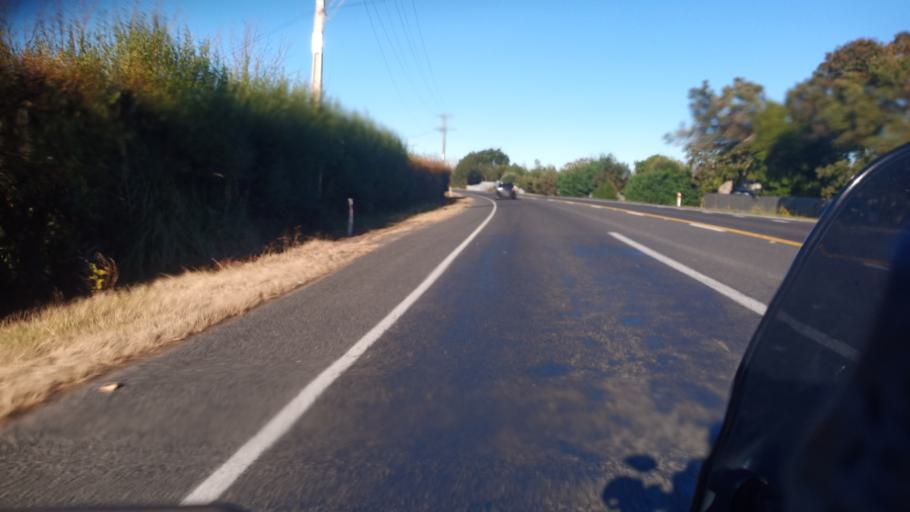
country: NZ
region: Hawke's Bay
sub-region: Napier City
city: Napier
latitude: -39.4188
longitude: 176.8677
